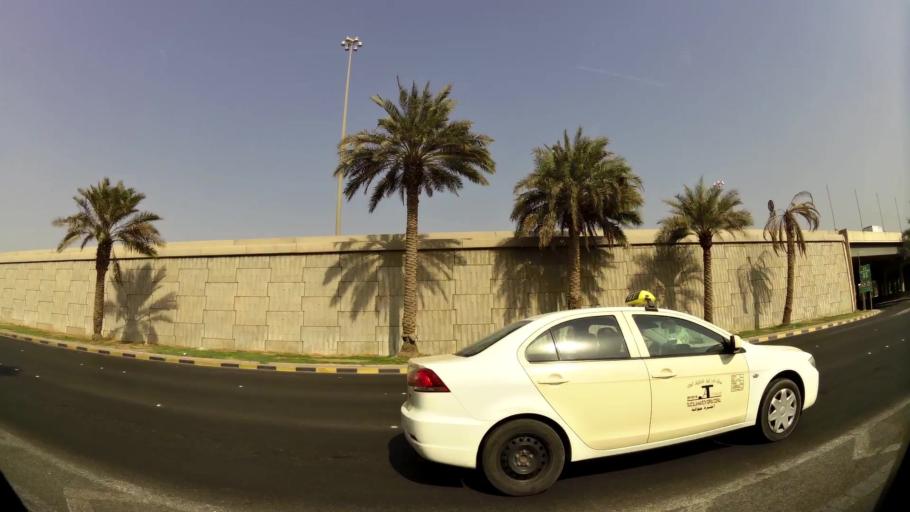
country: KW
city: Bayan
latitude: 29.3044
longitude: 48.0601
